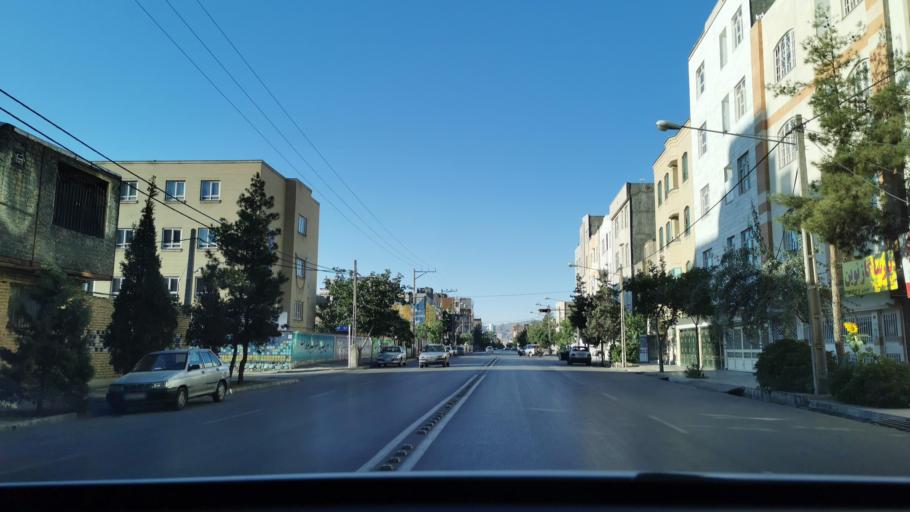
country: IR
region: Razavi Khorasan
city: Mashhad
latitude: 36.3559
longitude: 59.4972
